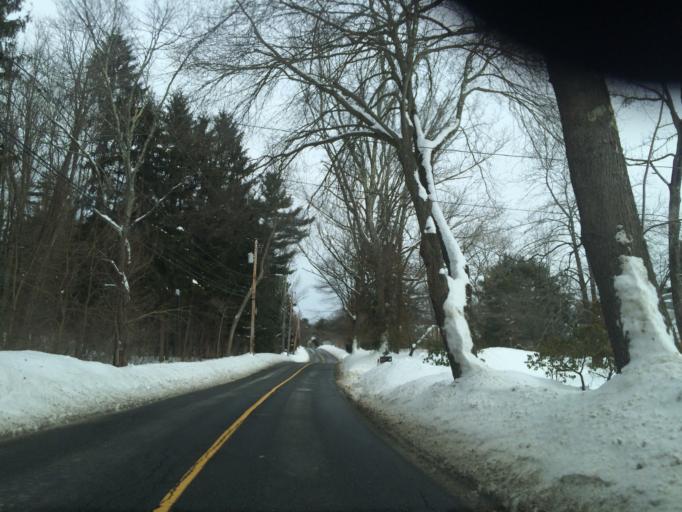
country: US
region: Massachusetts
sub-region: Middlesex County
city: Weston
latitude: 42.3350
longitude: -71.2894
